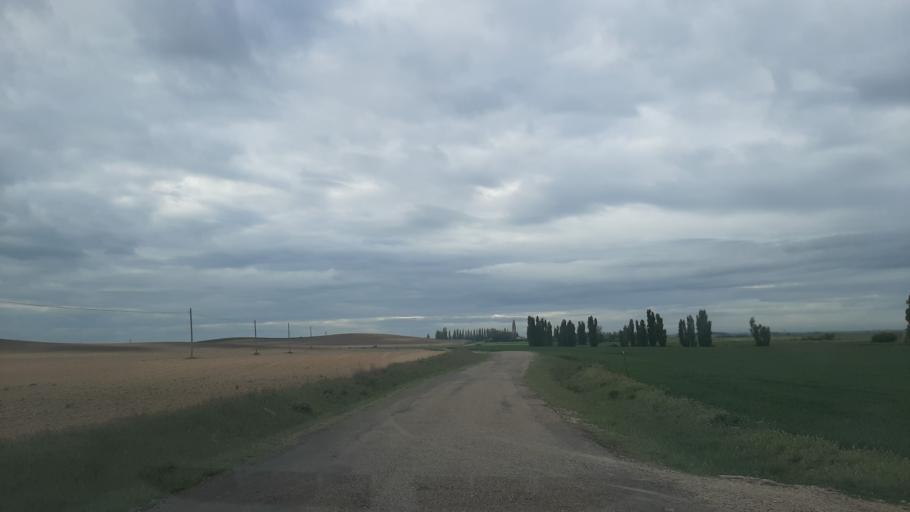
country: ES
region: Castille and Leon
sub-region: Provincia de Salamanca
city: Palaciosrubios
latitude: 41.0646
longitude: -5.2023
